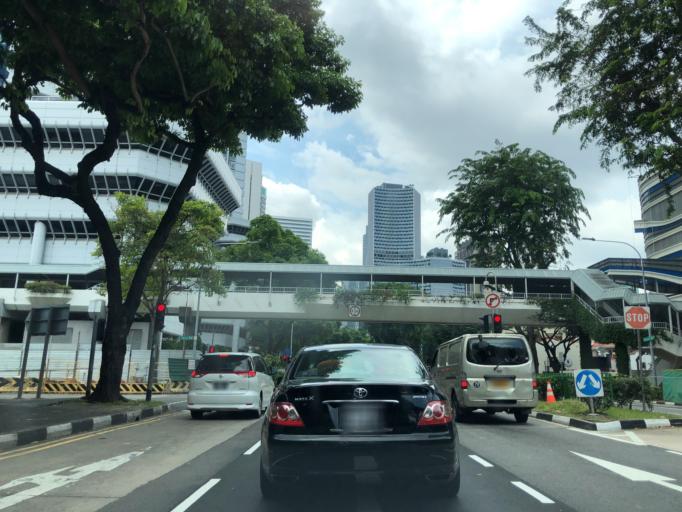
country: SG
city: Singapore
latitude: 1.3020
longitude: 103.8631
